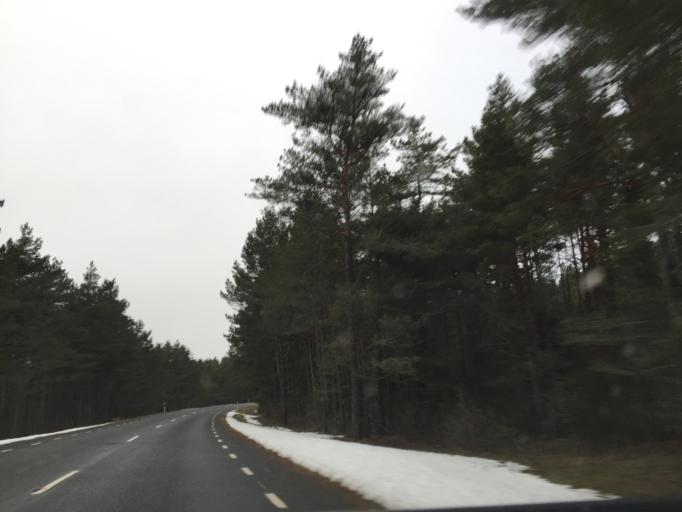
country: EE
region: Saare
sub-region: Kuressaare linn
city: Kuressaare
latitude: 58.5547
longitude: 22.3175
